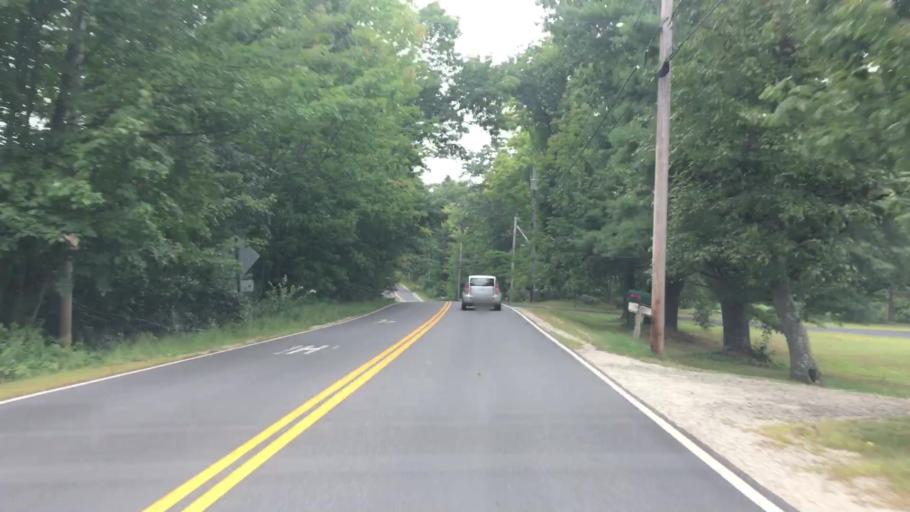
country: US
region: Maine
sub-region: Cumberland County
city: Cumberland Center
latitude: 43.8756
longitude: -70.2447
